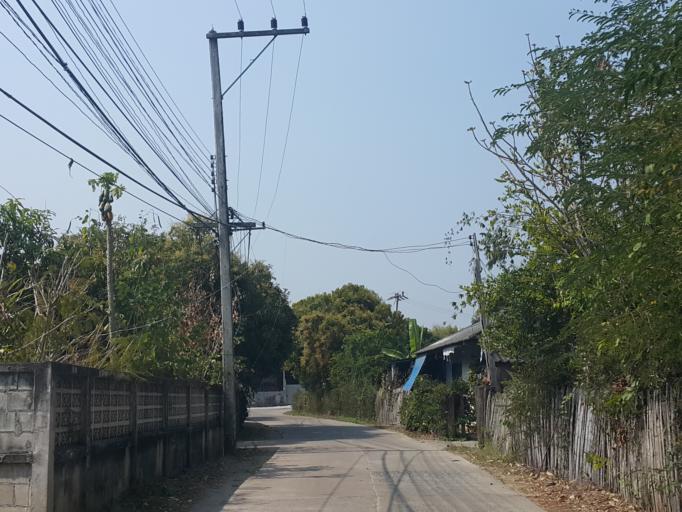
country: TH
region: Chiang Mai
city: Mae Taeng
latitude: 18.9542
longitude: 98.9187
